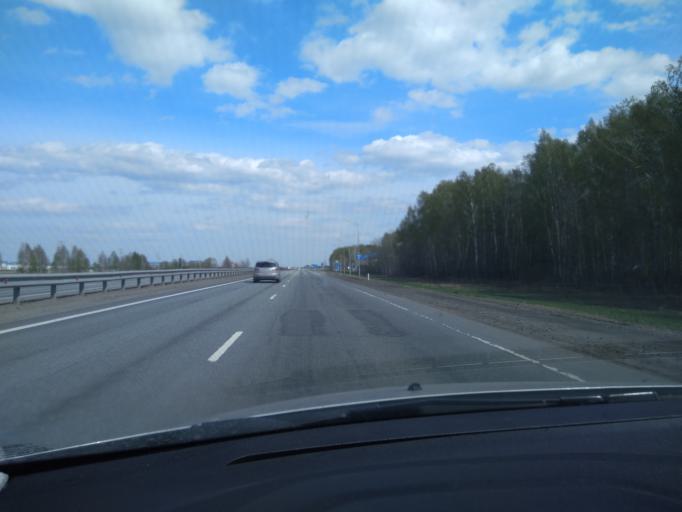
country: RU
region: Sverdlovsk
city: Zavodouspenskoye
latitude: 57.0936
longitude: 65.1491
